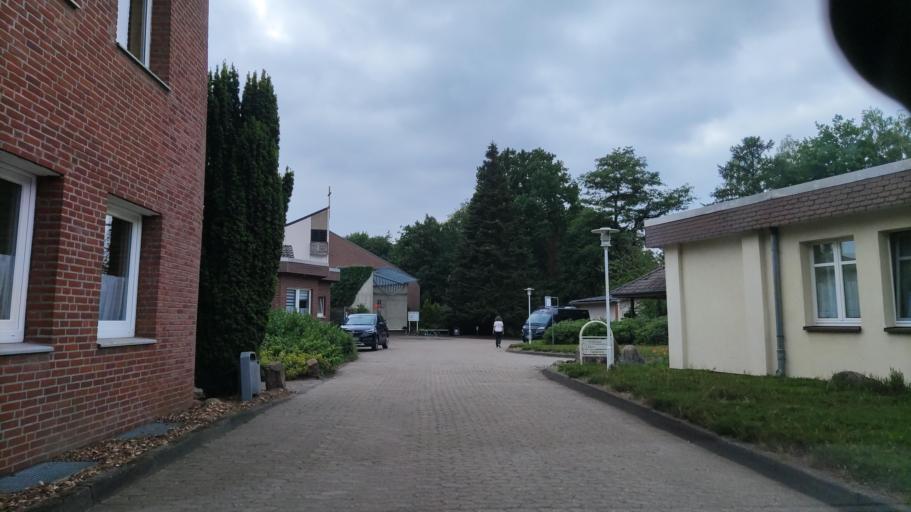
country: DE
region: Lower Saxony
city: Bad Fallingbostel
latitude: 52.8057
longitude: 9.6510
